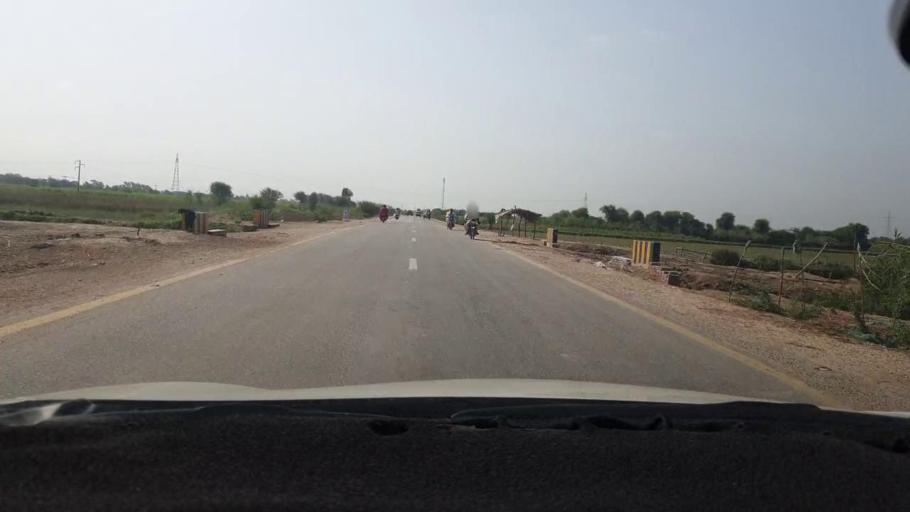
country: PK
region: Sindh
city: Tando Mittha Khan
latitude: 25.8354
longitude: 69.0630
